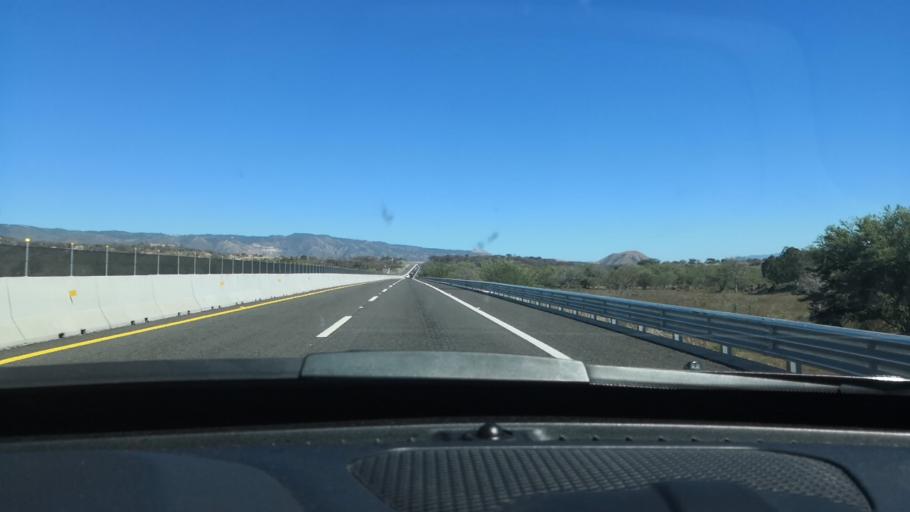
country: MX
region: Nayarit
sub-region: Ahuacatlan
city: Ahuacatlan
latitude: 21.0664
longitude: -104.4810
